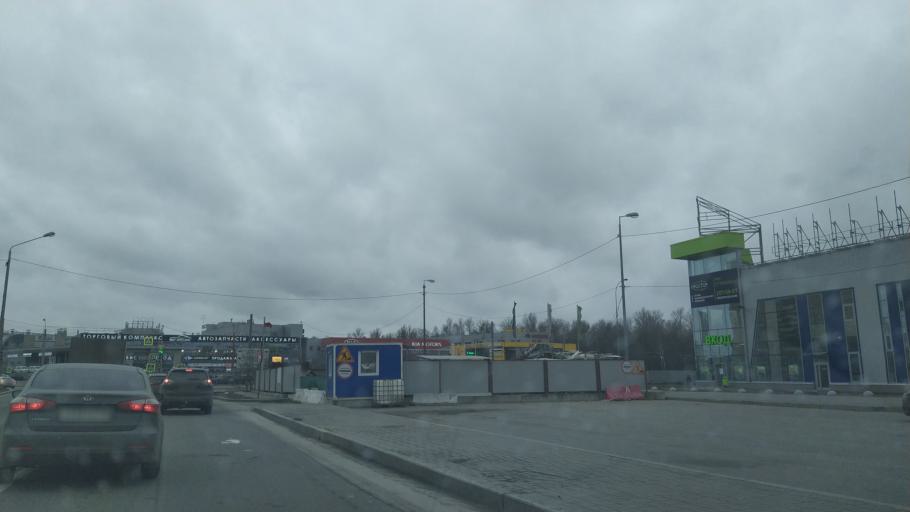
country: RU
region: St.-Petersburg
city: Komendantsky aerodrom
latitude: 60.0004
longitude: 30.2697
